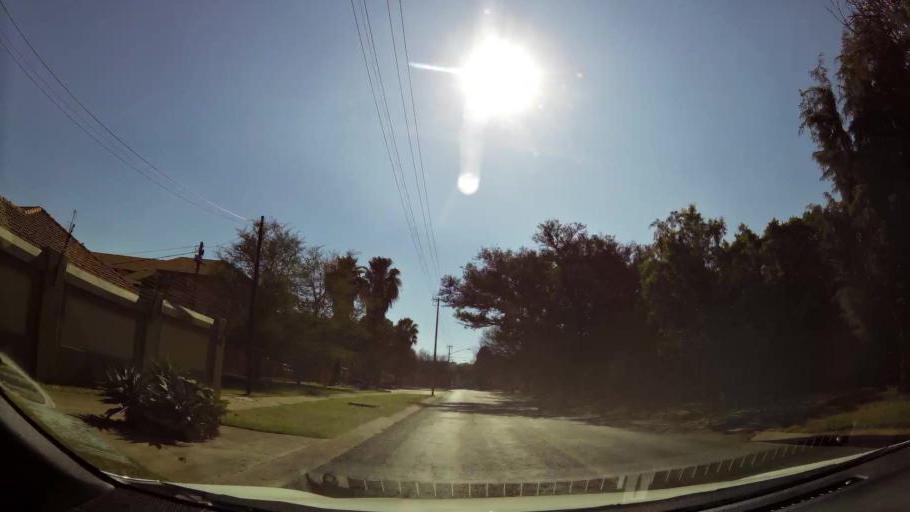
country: ZA
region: Gauteng
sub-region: City of Tshwane Metropolitan Municipality
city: Pretoria
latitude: -25.8025
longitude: 28.2318
